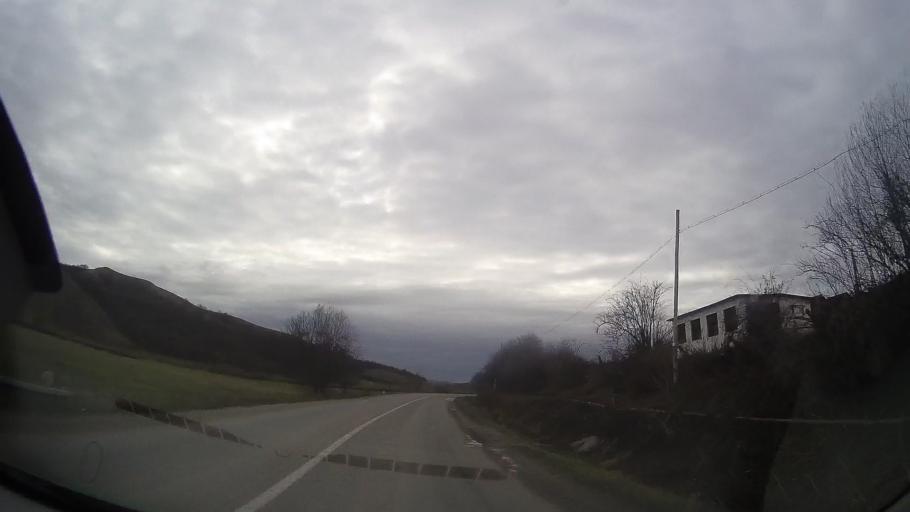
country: RO
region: Bistrita-Nasaud
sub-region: Comuna Budesti
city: Budesti
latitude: 46.8662
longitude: 24.2465
